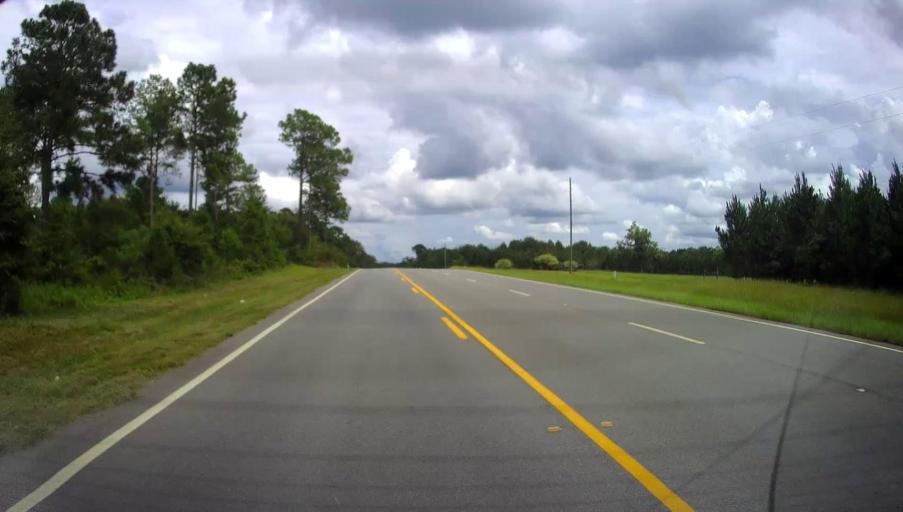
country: US
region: Georgia
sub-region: Macon County
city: Oglethorpe
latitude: 32.2828
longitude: -84.1533
